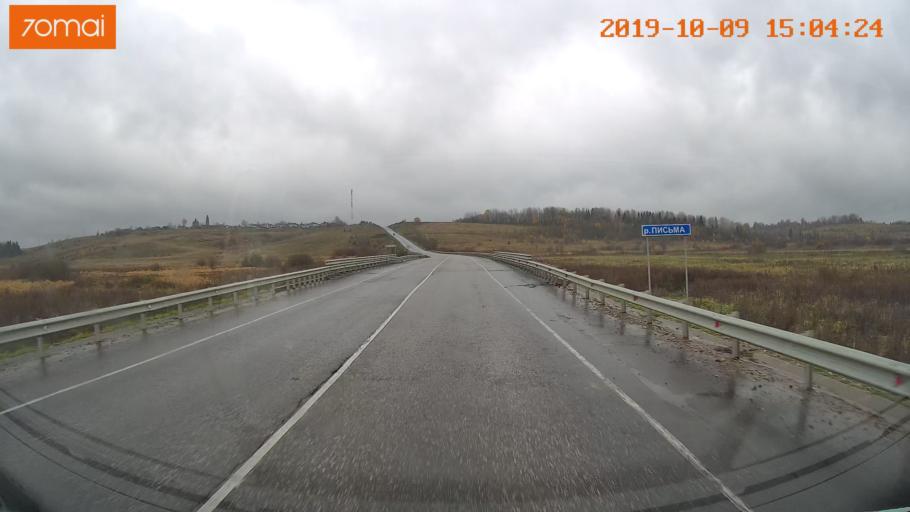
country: RU
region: Kostroma
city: Chistyye Bory
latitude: 58.2590
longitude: 41.6675
